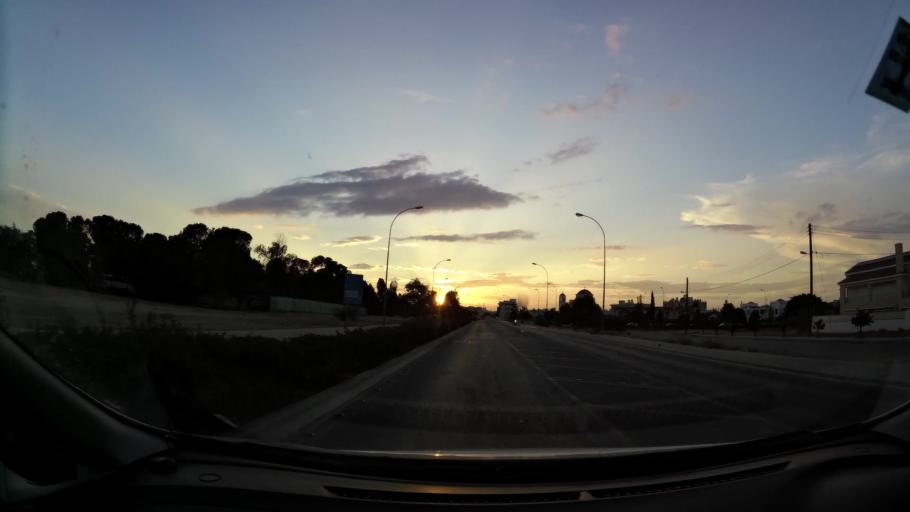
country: CY
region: Lefkosia
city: Nicosia
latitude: 35.1486
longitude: 33.3825
